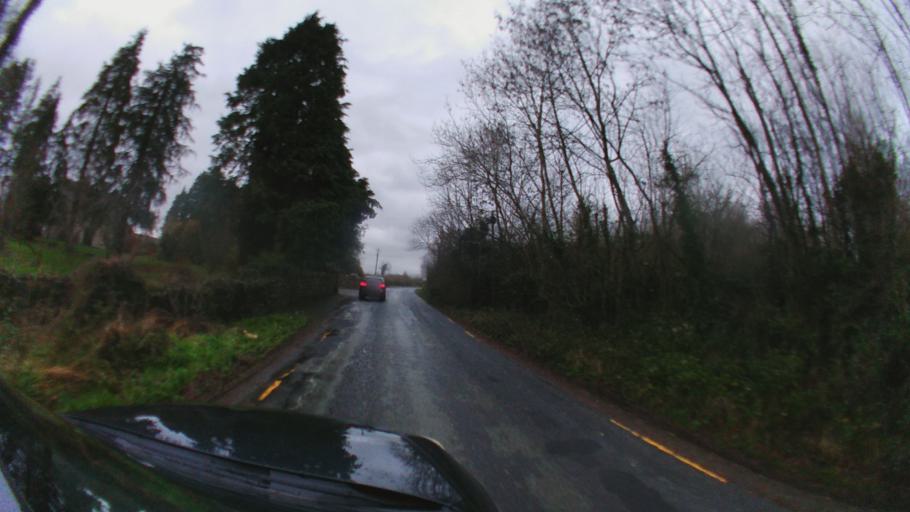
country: IE
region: Leinster
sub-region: Kilkenny
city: Graiguenamanagh
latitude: 52.6179
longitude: -6.9903
